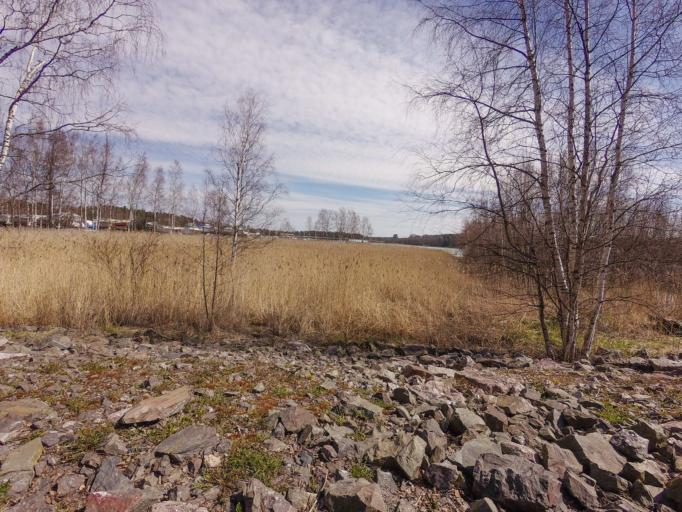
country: FI
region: Uusimaa
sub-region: Helsinki
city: Vantaa
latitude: 60.2042
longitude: 25.0959
